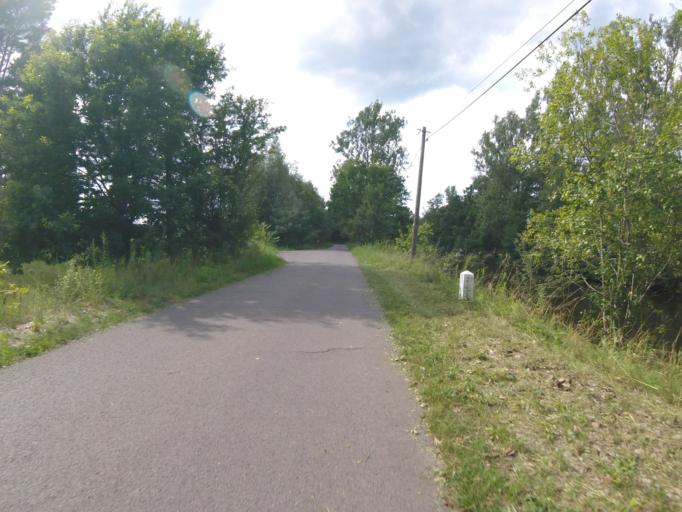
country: DE
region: Brandenburg
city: Halbe
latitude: 52.0987
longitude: 13.7751
